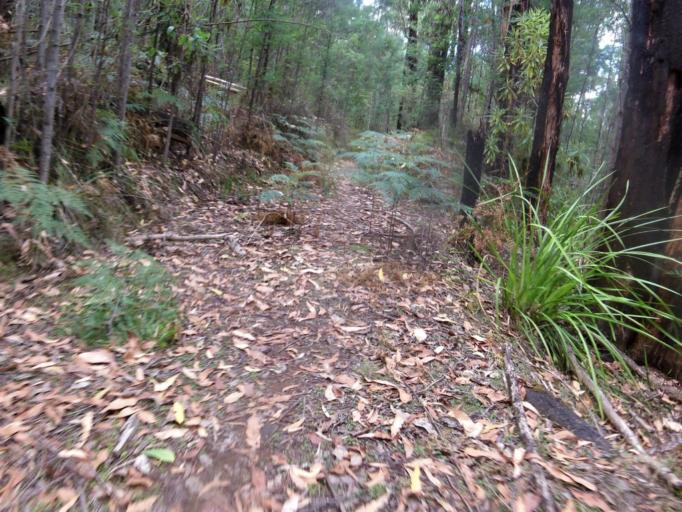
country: AU
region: Victoria
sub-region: Yarra Ranges
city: Healesville
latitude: -37.4273
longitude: 145.5752
